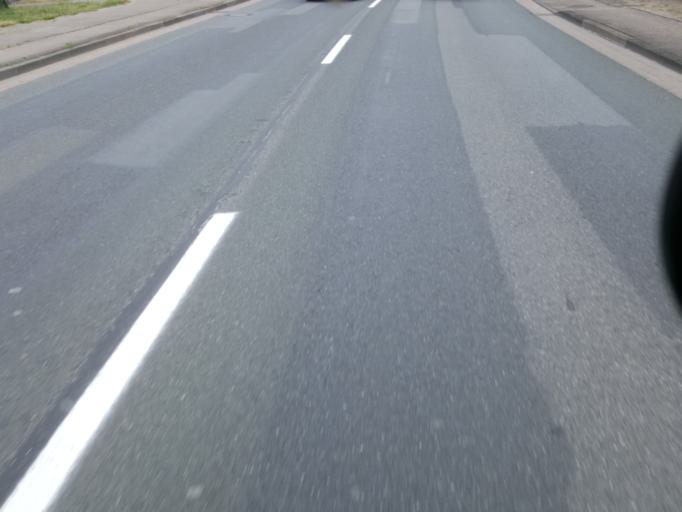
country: DE
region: Lower Saxony
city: Leese
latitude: 52.5018
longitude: 9.1174
